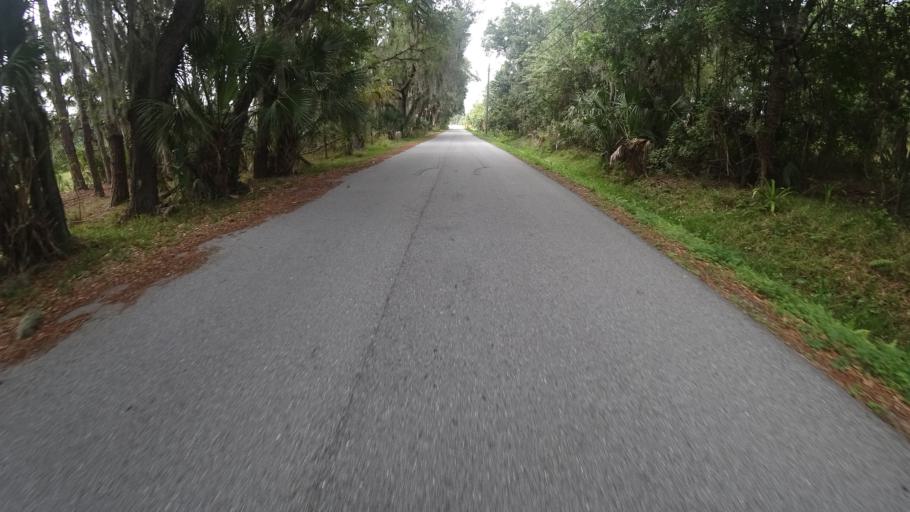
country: US
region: Florida
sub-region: Sarasota County
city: North Sarasota
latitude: 27.3986
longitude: -82.5301
